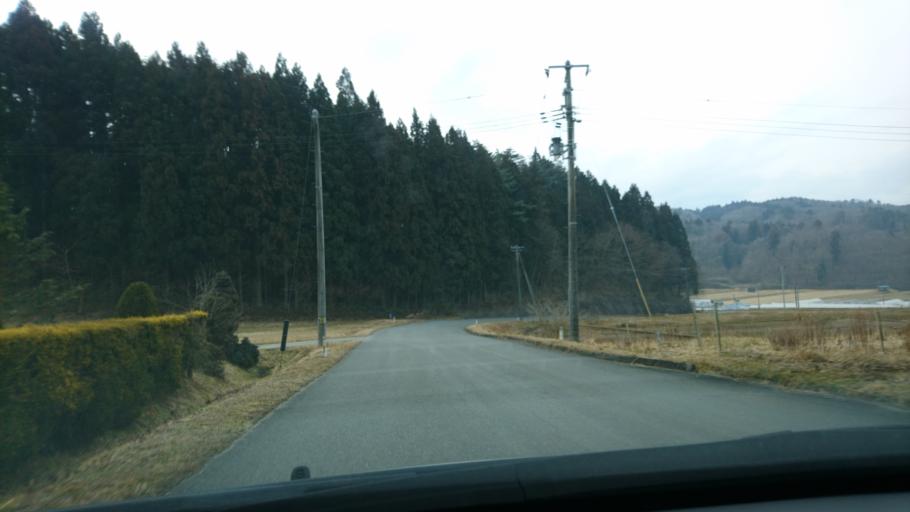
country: JP
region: Iwate
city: Ichinoseki
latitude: 38.8912
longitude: 141.3787
